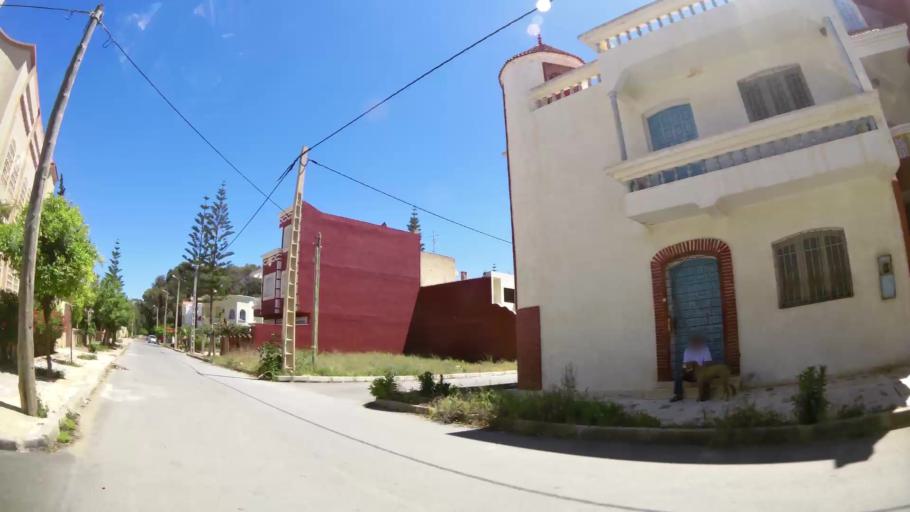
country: MA
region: Oriental
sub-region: Berkane-Taourirt
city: Madagh
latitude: 35.0854
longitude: -2.2375
